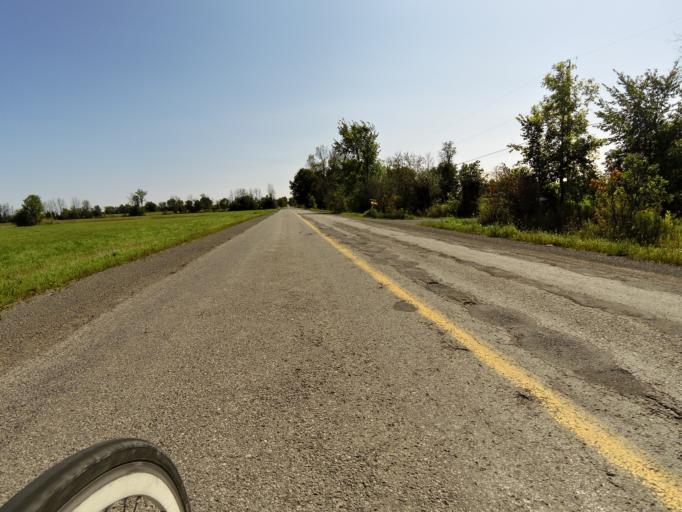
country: CA
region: Ontario
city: Bells Corners
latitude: 45.4294
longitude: -76.0556
